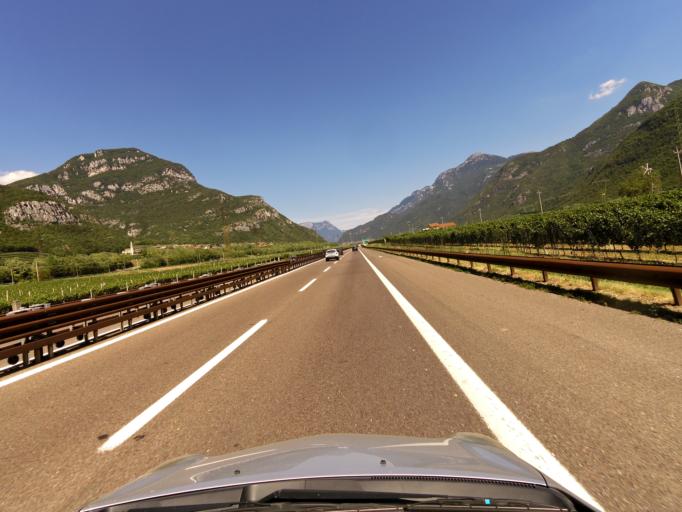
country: IT
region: Veneto
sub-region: Provincia di Verona
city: Rivalta
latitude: 45.6329
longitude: 10.8714
